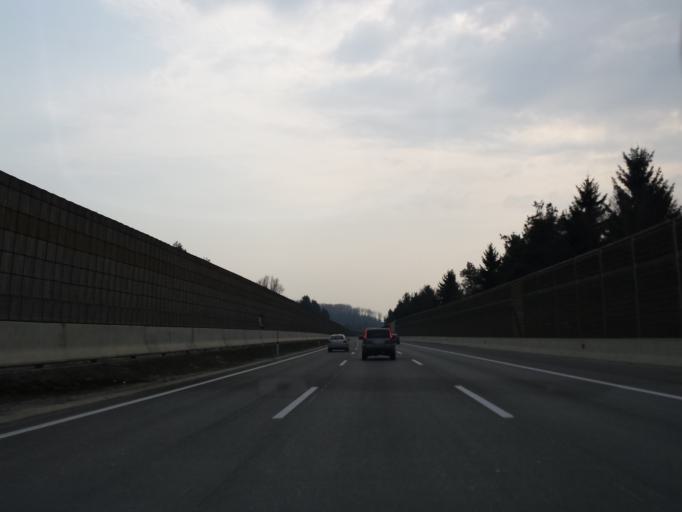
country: AT
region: Styria
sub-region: Politischer Bezirk Graz-Umgebung
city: Raaba
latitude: 47.0351
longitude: 15.5084
